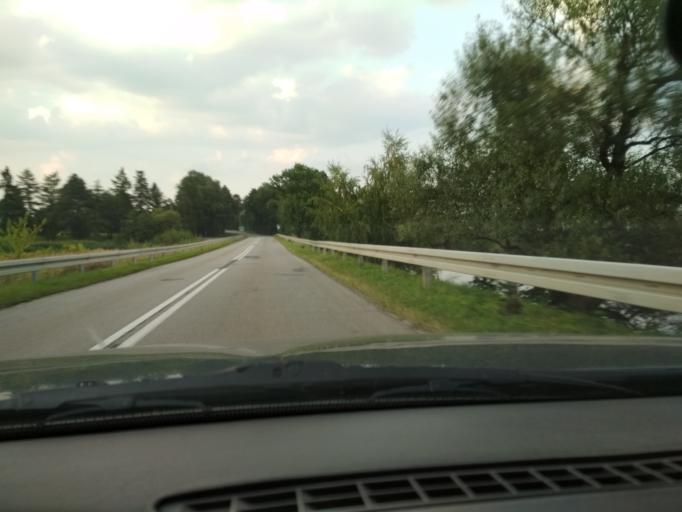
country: PL
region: Silesian Voivodeship
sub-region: Powiat cieszynski
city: Chybie
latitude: 49.9360
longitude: 18.8092
